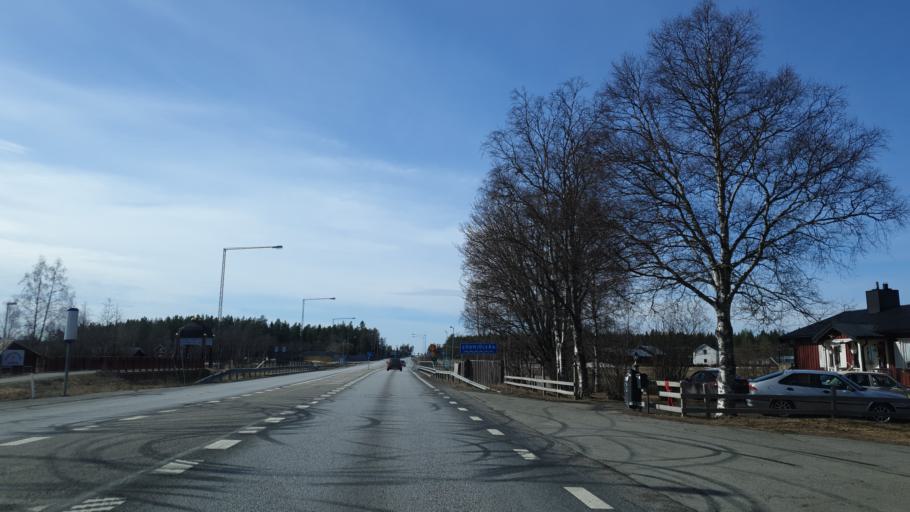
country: SE
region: Vaesterbotten
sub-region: Umea Kommun
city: Hoernefors
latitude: 63.6813
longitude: 19.9998
